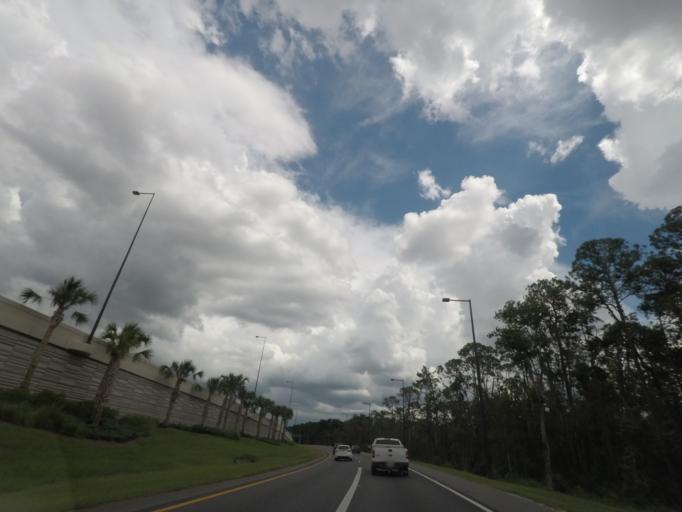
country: US
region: Florida
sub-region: Osceola County
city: Celebration
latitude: 28.3689
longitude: -81.5378
